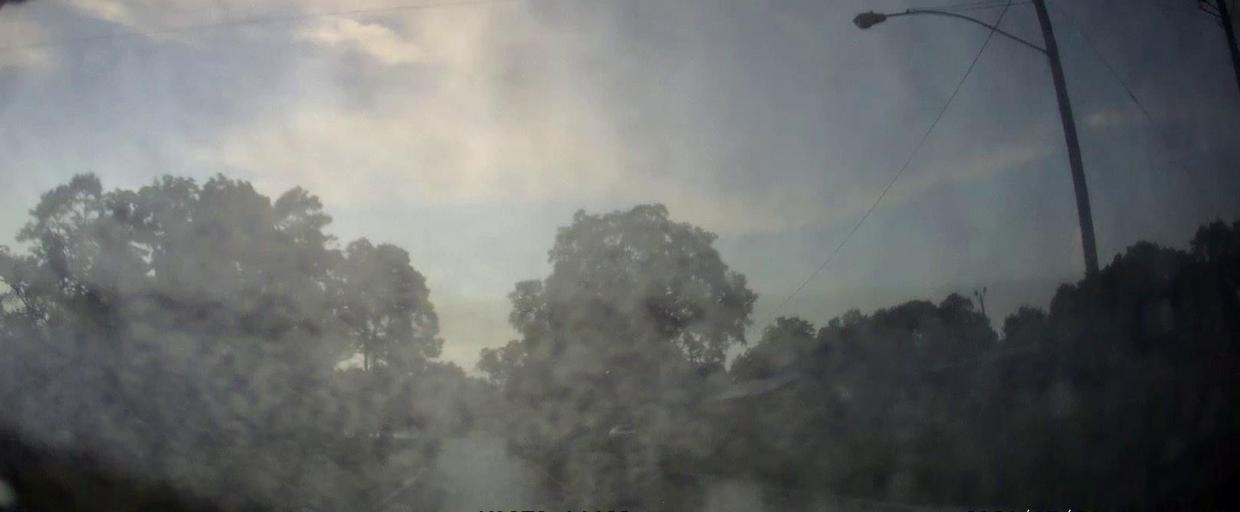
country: US
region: Georgia
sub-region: Dodge County
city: Chester
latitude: 32.5583
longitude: -83.1510
